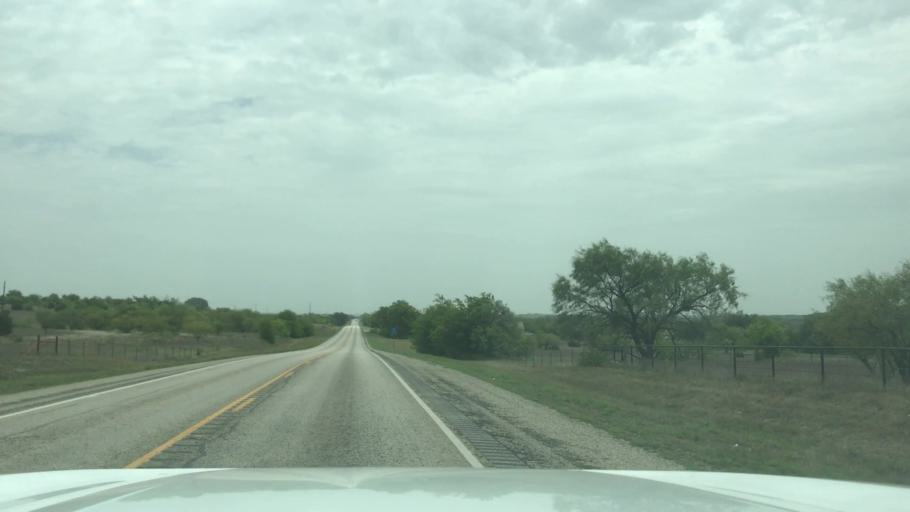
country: US
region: Texas
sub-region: Hamilton County
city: Hico
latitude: 32.0511
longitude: -98.1642
